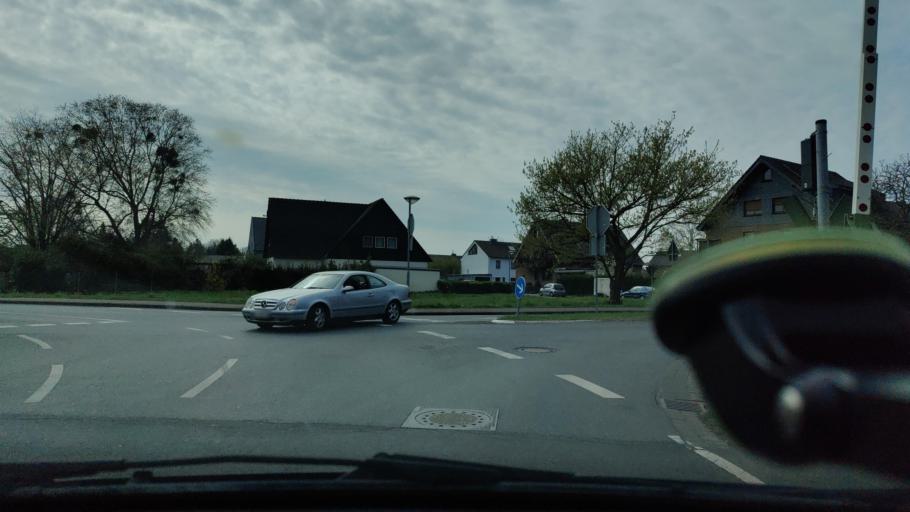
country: DE
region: North Rhine-Westphalia
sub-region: Regierungsbezirk Dusseldorf
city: Dinslaken
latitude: 51.5229
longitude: 6.6809
